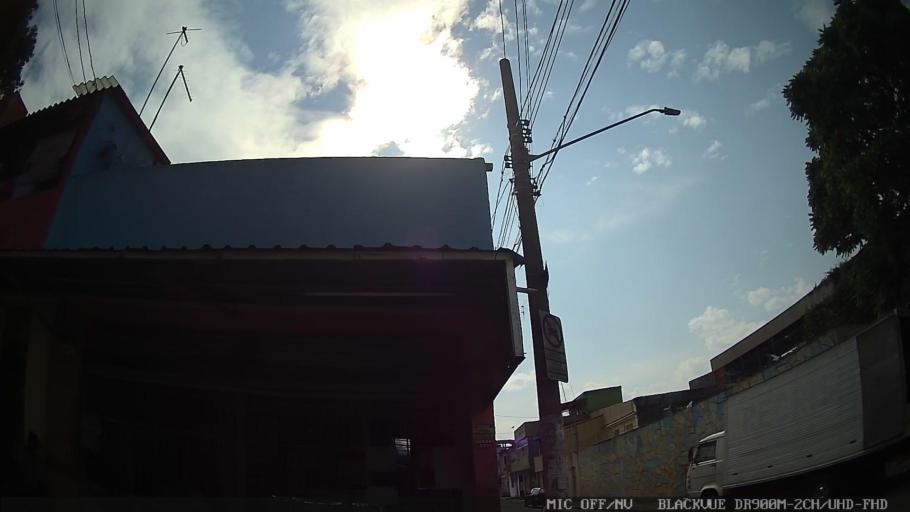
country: BR
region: Sao Paulo
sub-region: Ferraz De Vasconcelos
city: Ferraz de Vasconcelos
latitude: -23.4950
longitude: -46.4151
